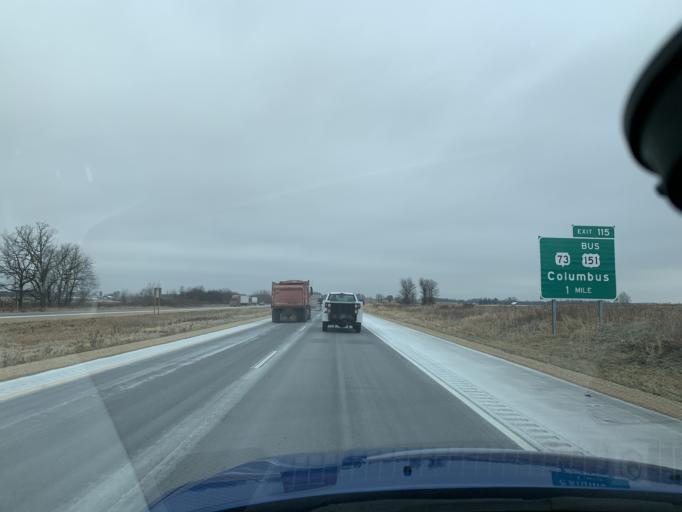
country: US
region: Wisconsin
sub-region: Columbia County
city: Columbus
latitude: 43.3002
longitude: -89.0572
